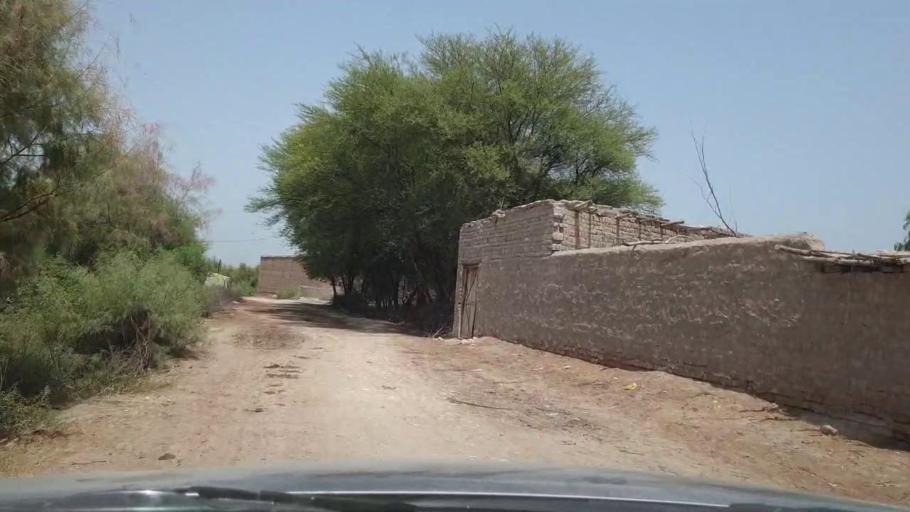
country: PK
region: Sindh
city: Pano Aqil
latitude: 27.8655
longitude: 69.1818
